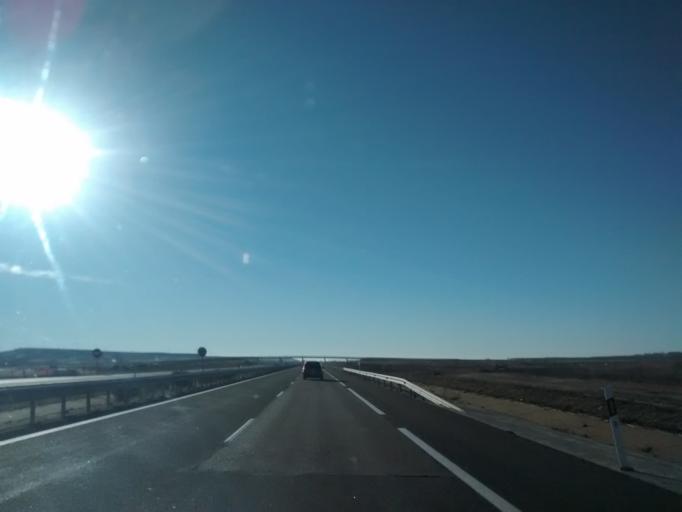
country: ES
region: Castille and Leon
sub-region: Provincia de Palencia
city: Santa Cruz de Boedo
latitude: 42.5190
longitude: -4.3830
